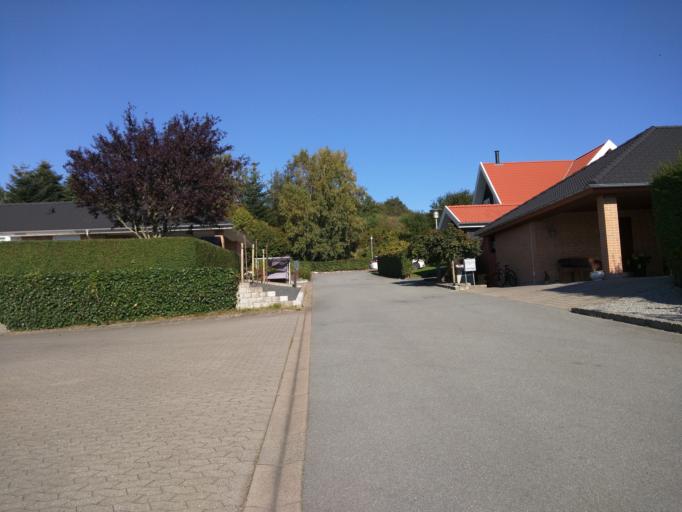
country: DK
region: Central Jutland
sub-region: Viborg Kommune
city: Viborg
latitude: 56.4342
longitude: 9.3820
